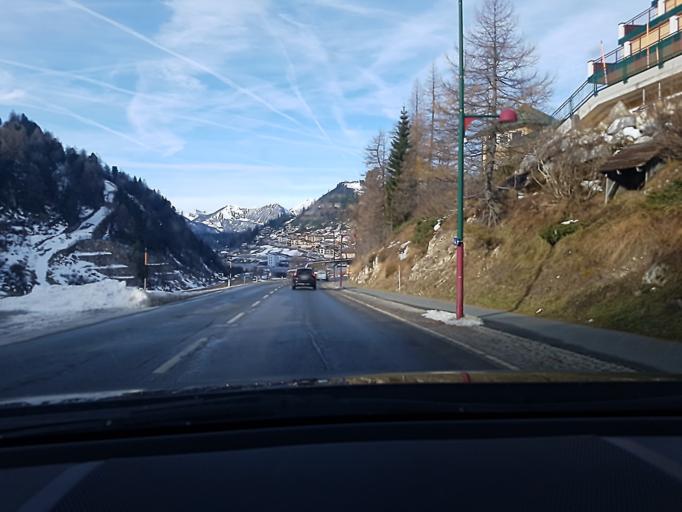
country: AT
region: Salzburg
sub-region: Politischer Bezirk Sankt Johann im Pongau
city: Untertauern
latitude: 47.2505
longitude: 13.5512
